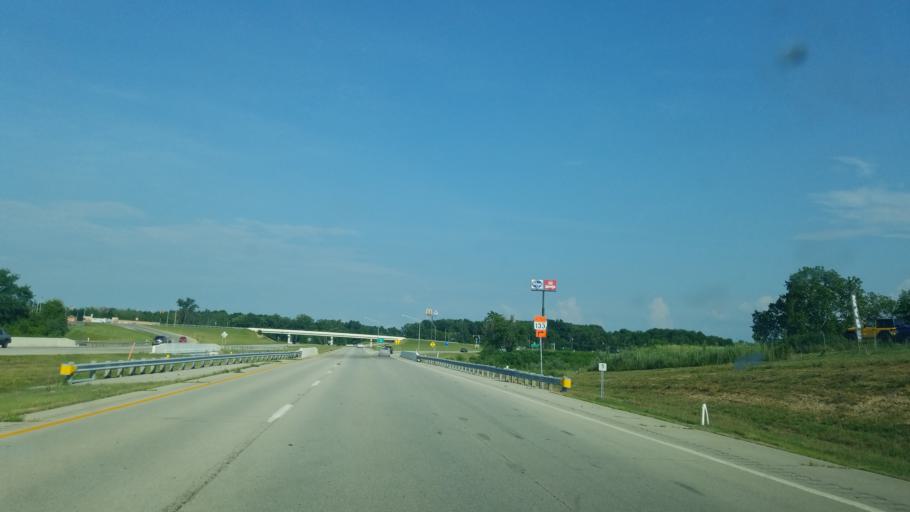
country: US
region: Ohio
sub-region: Brown County
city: Mount Orab
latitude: 39.0427
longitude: -83.9253
